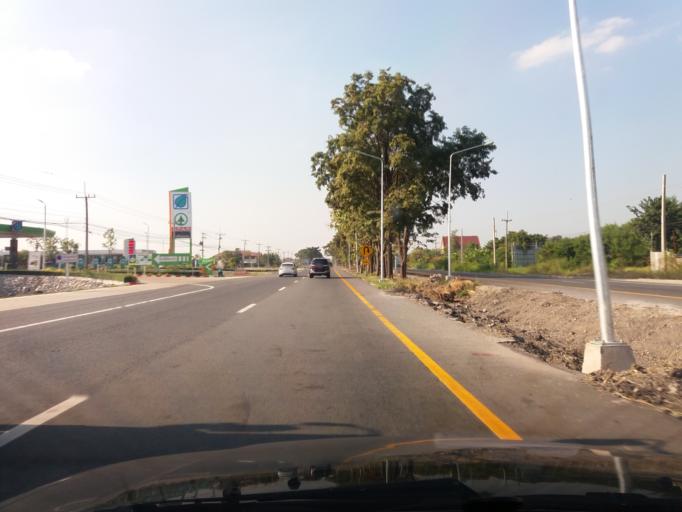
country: TH
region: Nakhon Sawan
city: Banphot Phisai
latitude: 15.8182
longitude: 99.9416
